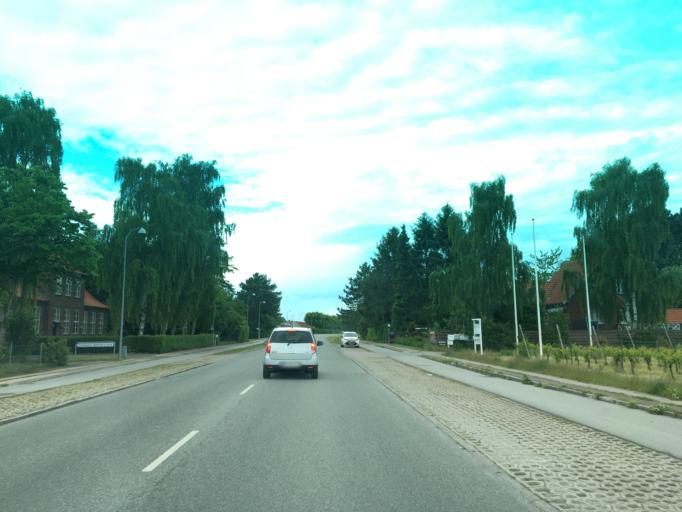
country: DK
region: Capital Region
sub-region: Hvidovre Kommune
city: Hvidovre
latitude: 55.6399
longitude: 12.4471
